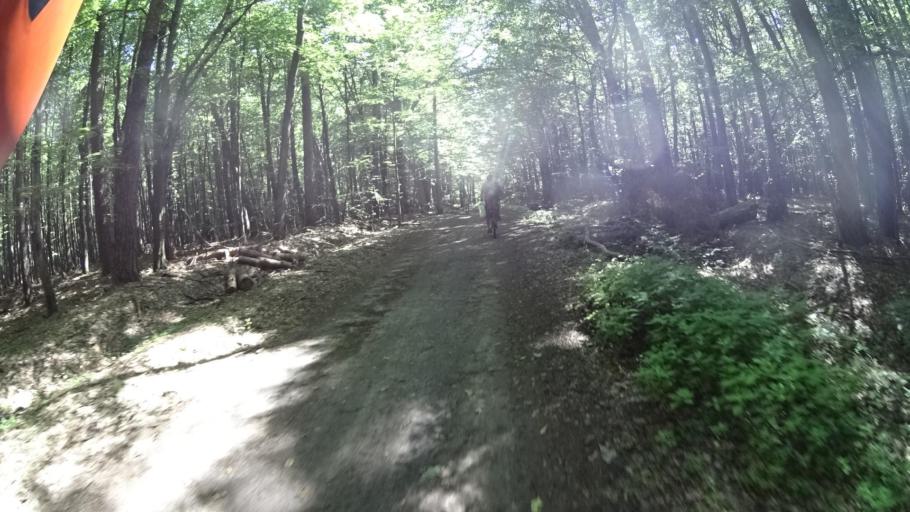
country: PL
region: Masovian Voivodeship
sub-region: Powiat piaseczynski
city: Jozefoslaw
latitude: 52.1195
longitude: 21.0551
